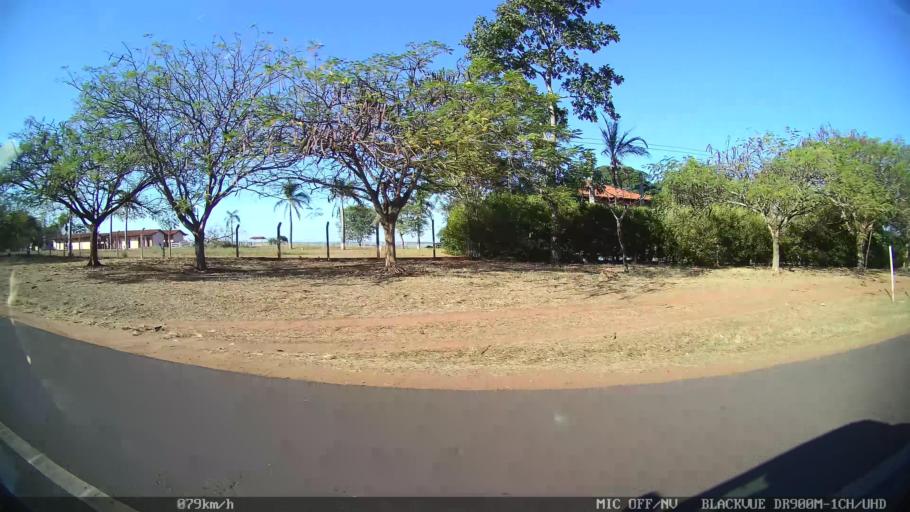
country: BR
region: Sao Paulo
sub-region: Olimpia
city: Olimpia
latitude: -20.7167
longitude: -48.9076
